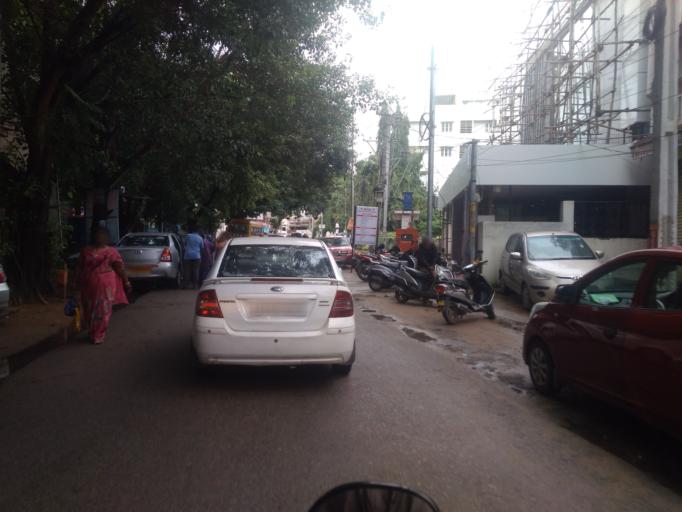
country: IN
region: Telangana
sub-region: Rangareddi
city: Secunderabad
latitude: 17.5037
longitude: 78.5126
